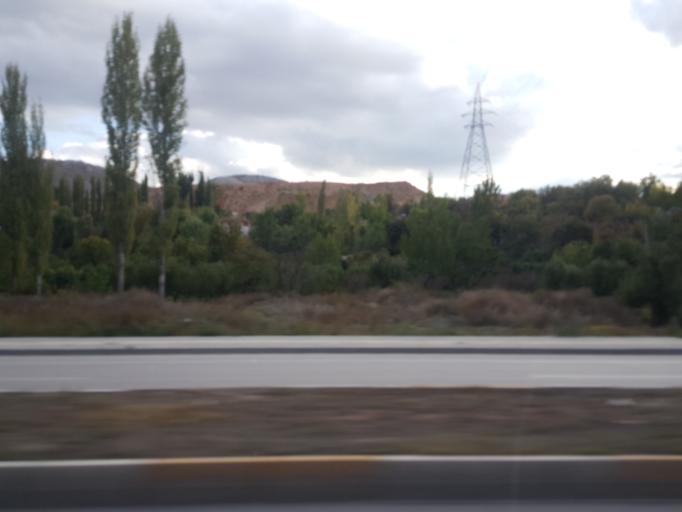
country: TR
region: Tokat
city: Tokat
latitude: 40.3377
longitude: 36.4998
